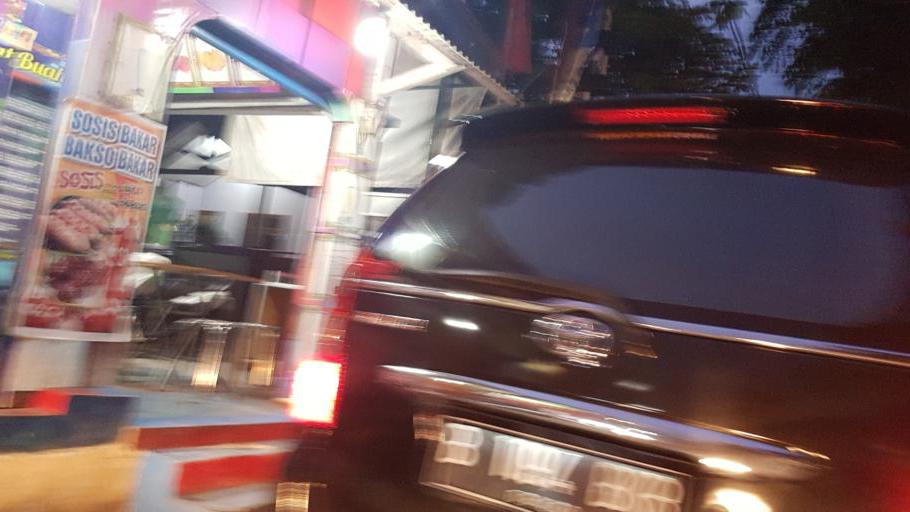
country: ID
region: West Java
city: Pamulang
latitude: -6.3426
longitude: 106.7970
